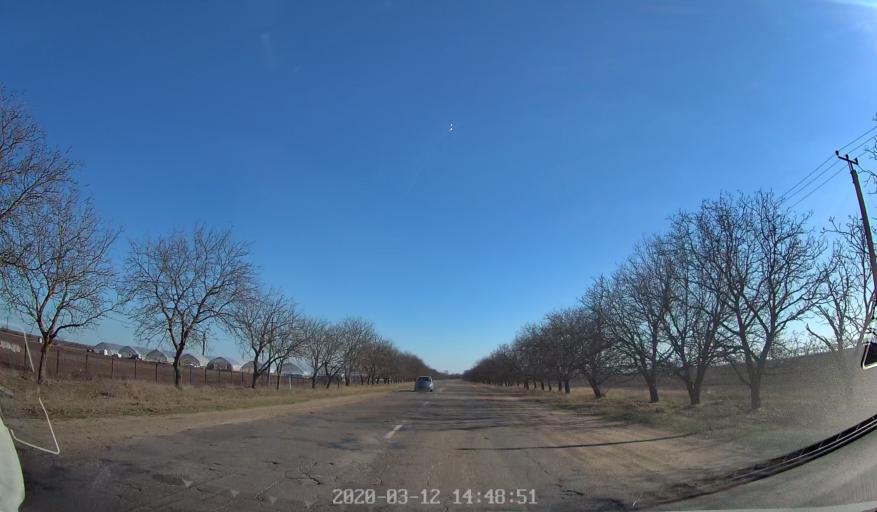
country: MD
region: Criuleni
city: Criuleni
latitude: 47.2290
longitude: 29.1417
